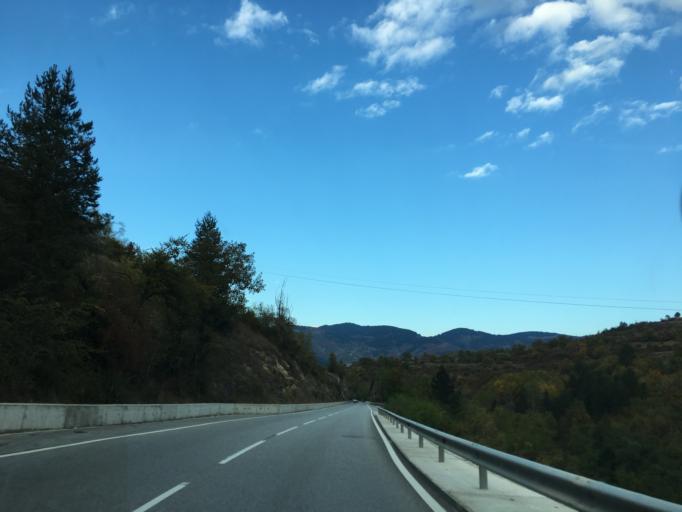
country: BG
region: Smolyan
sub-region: Obshtina Chepelare
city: Chepelare
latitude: 41.8542
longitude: 24.6846
